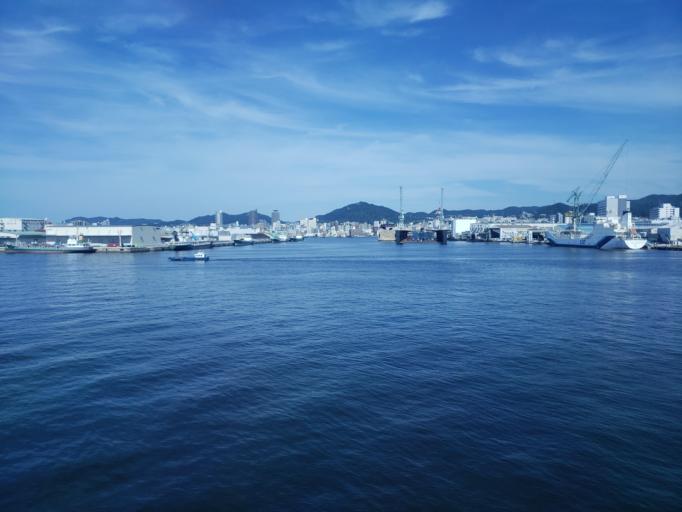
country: JP
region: Hyogo
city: Kobe
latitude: 34.6677
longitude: 135.1915
